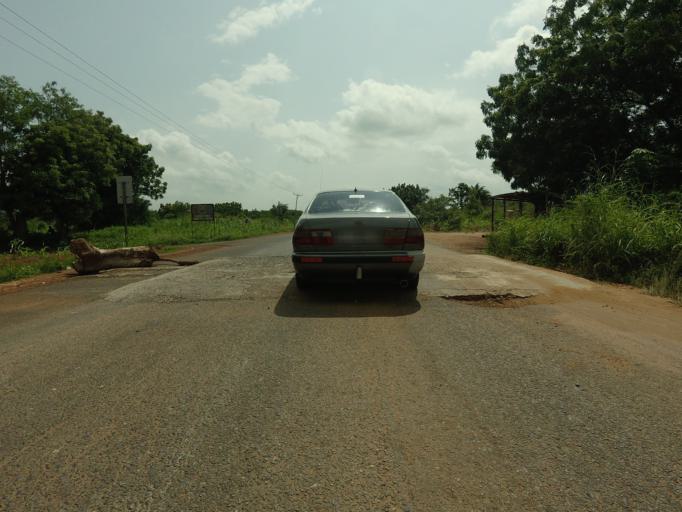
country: TG
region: Maritime
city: Lome
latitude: 6.2285
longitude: 1.0144
